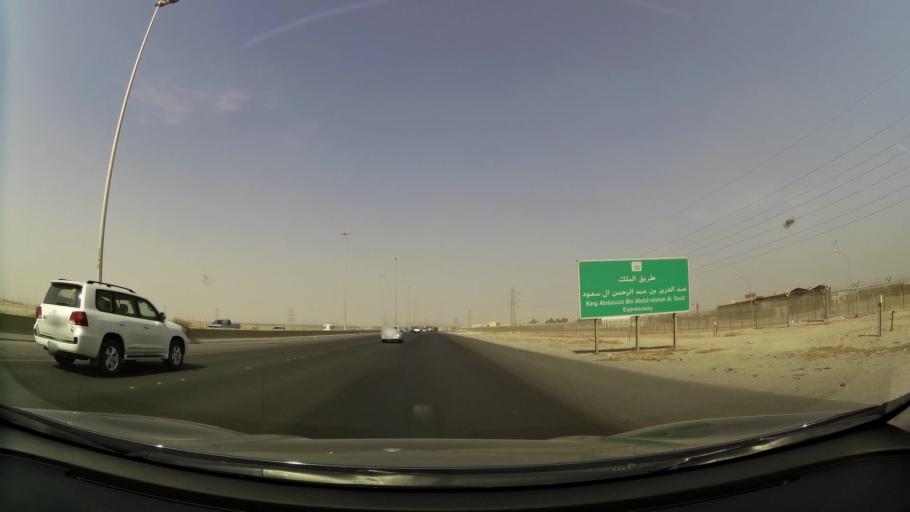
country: KW
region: Al Ahmadi
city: Al Fahahil
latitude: 29.0291
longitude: 48.1228
